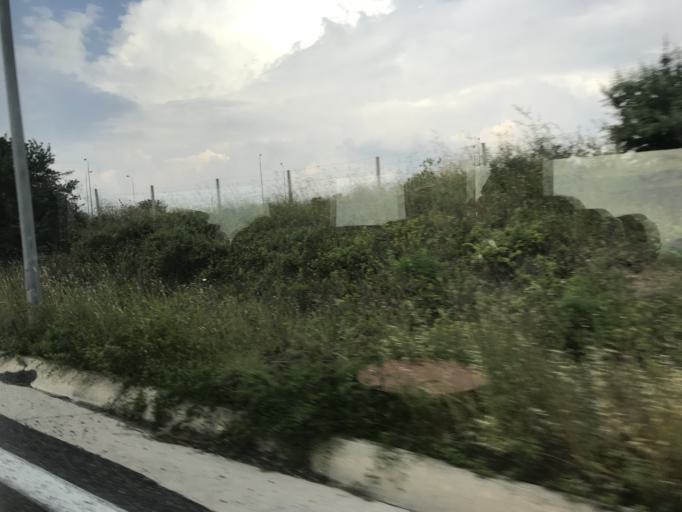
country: GR
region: East Macedonia and Thrace
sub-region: Nomos Rodopis
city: Sapes
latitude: 40.9628
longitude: 25.6433
